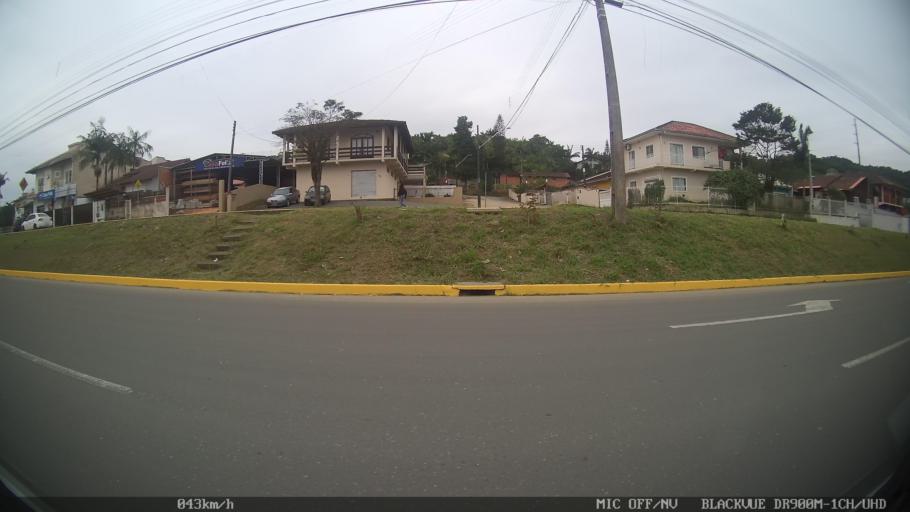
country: BR
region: Santa Catarina
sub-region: Joinville
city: Joinville
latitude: -26.3620
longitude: -48.8078
